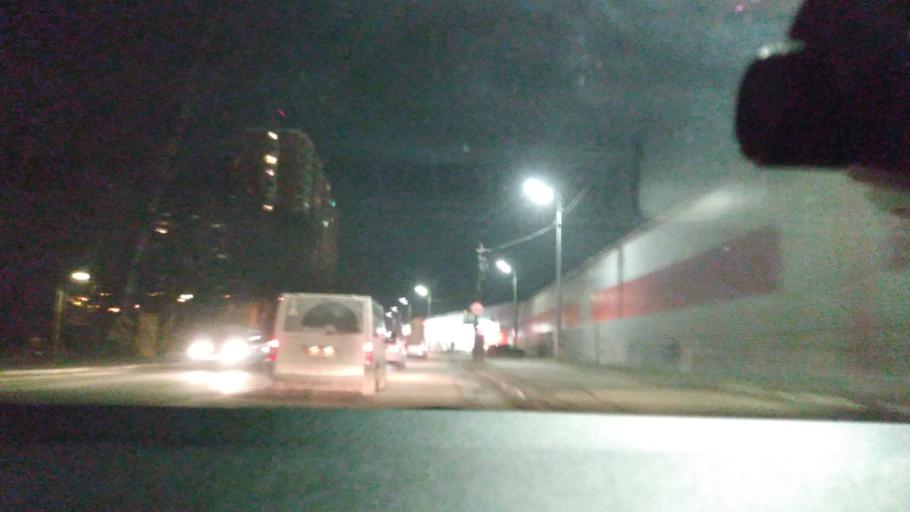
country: RU
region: Moskovskaya
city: Balashikha
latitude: 55.8190
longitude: 37.9530
